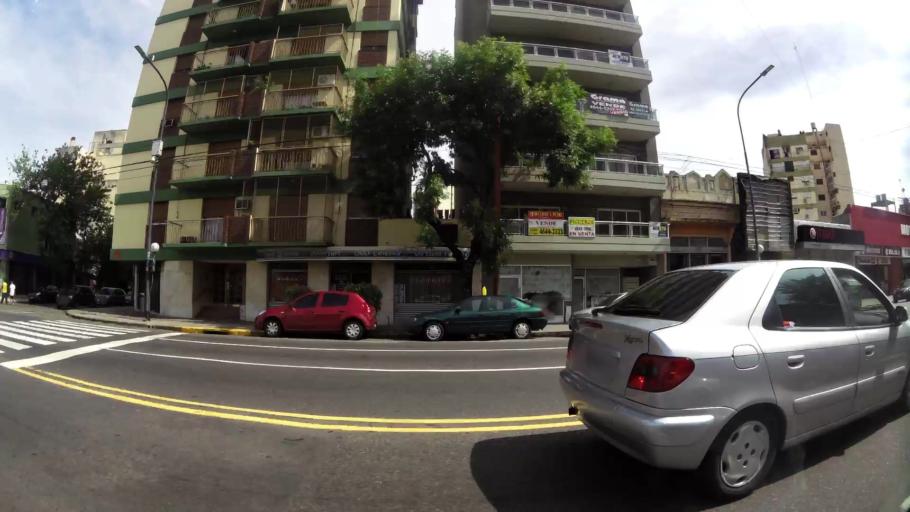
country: AR
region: Buenos Aires F.D.
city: Villa Santa Rita
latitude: -34.6392
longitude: -58.5147
